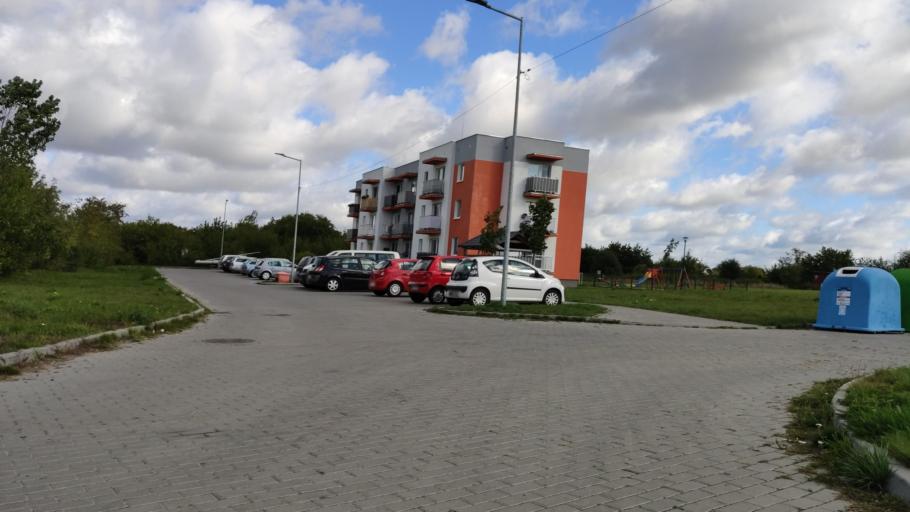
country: PL
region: Kujawsko-Pomorskie
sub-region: Powiat zninski
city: Znin
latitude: 52.8562
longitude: 17.7570
